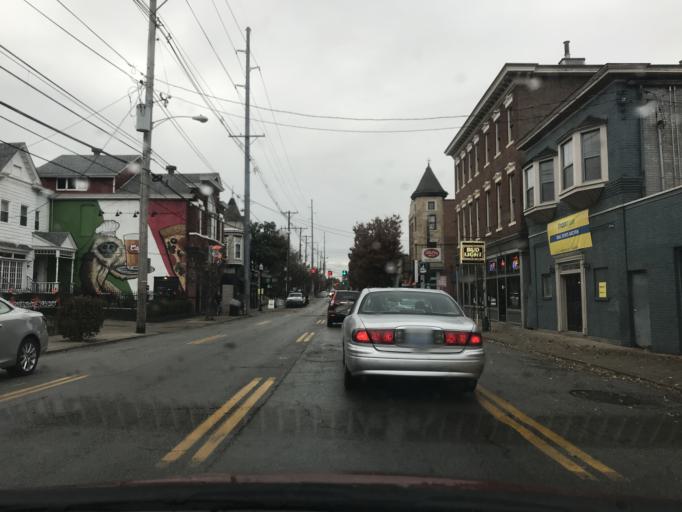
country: US
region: Kentucky
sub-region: Jefferson County
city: Louisville
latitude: 38.2425
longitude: -85.7261
